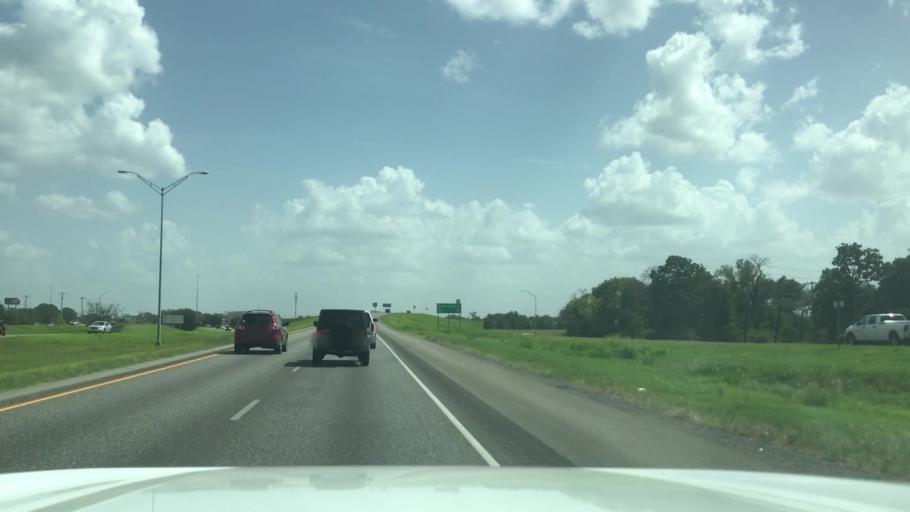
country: US
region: Texas
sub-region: Brazos County
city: College Station
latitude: 30.5983
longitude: -96.2904
